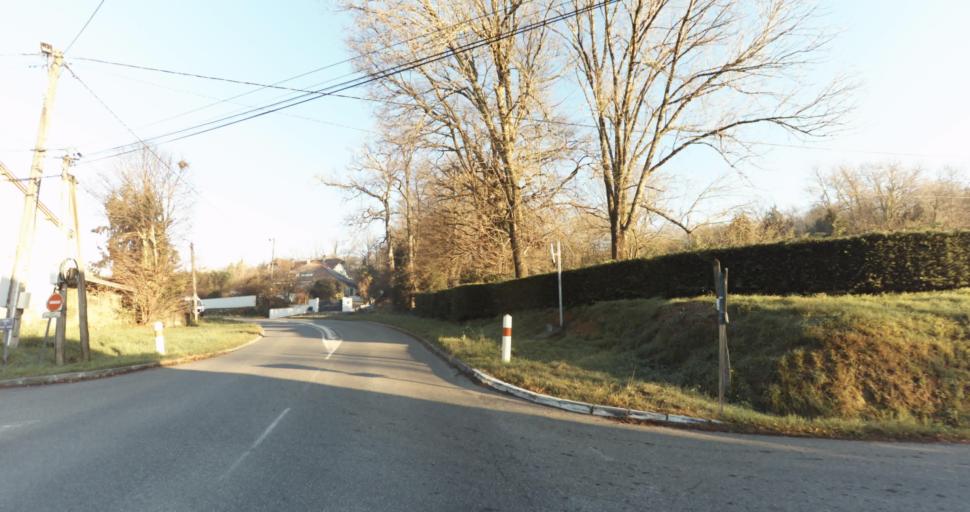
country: FR
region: Aquitaine
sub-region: Departement des Pyrenees-Atlantiques
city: Morlaas
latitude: 43.3278
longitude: -0.2736
